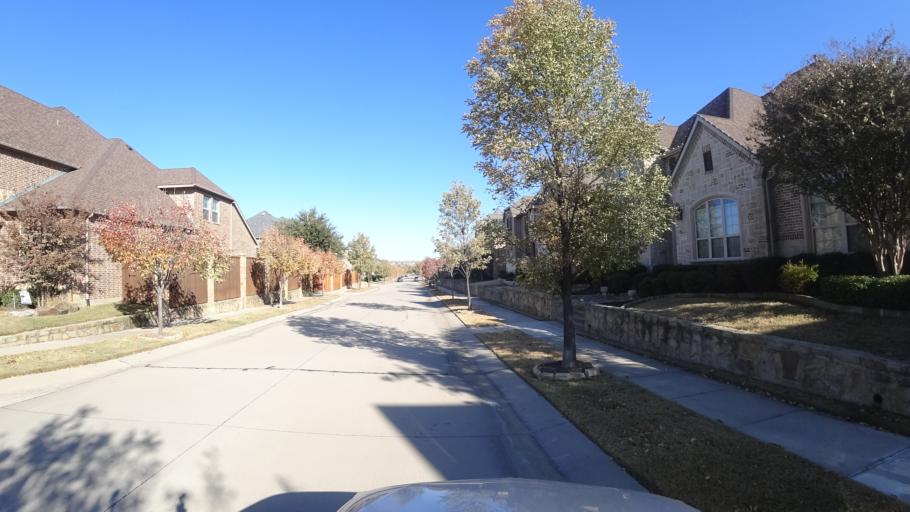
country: US
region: Texas
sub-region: Denton County
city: The Colony
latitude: 33.0413
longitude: -96.9192
